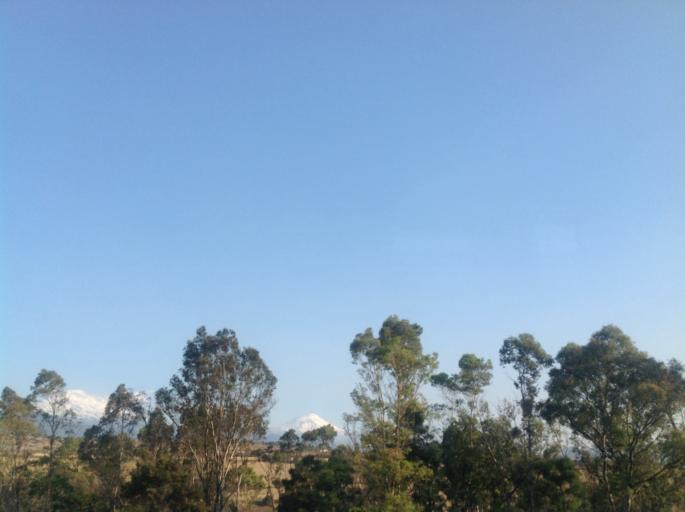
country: MX
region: Mexico
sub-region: Ixtapaluca
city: Jorge Jimenez Cantu
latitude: 19.3141
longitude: -98.8224
